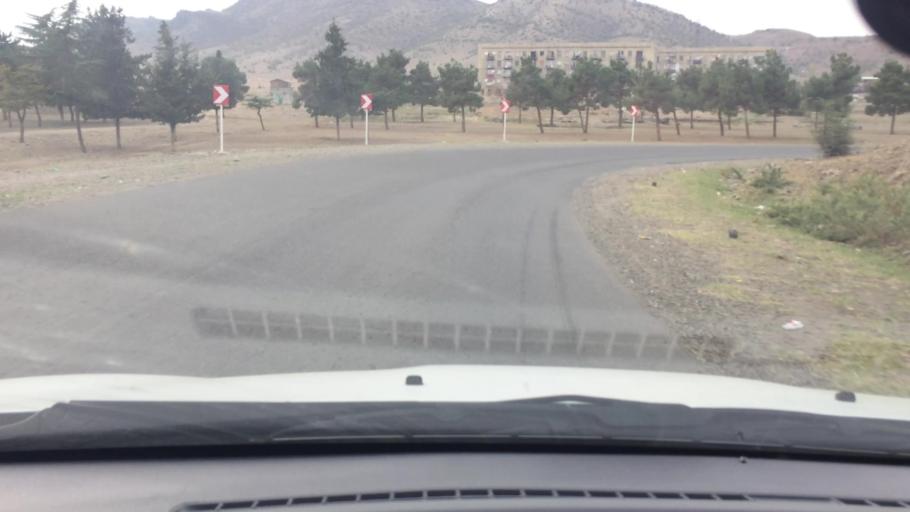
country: GE
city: Naghvarevi
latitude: 41.3604
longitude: 44.8375
